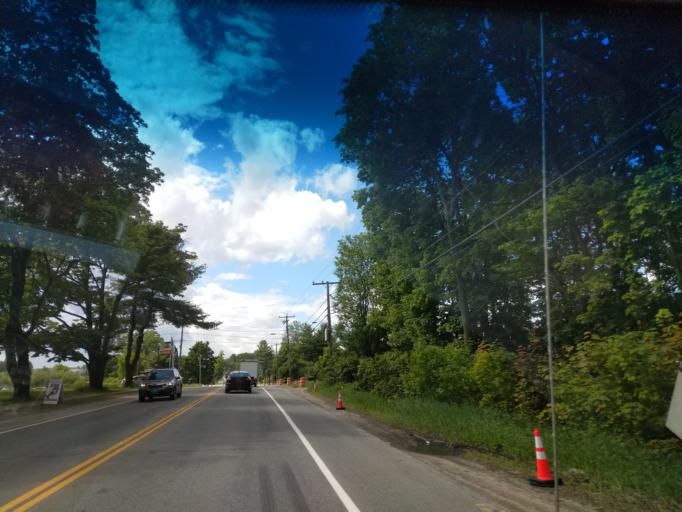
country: US
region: Maine
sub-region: Cumberland County
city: Westbrook
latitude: 43.6824
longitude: -70.3799
